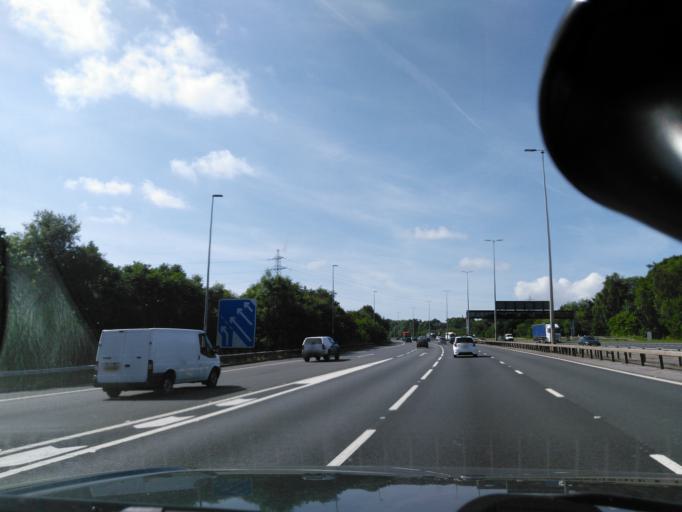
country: GB
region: England
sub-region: Hampshire
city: Hedge End
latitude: 50.9138
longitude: -1.3188
